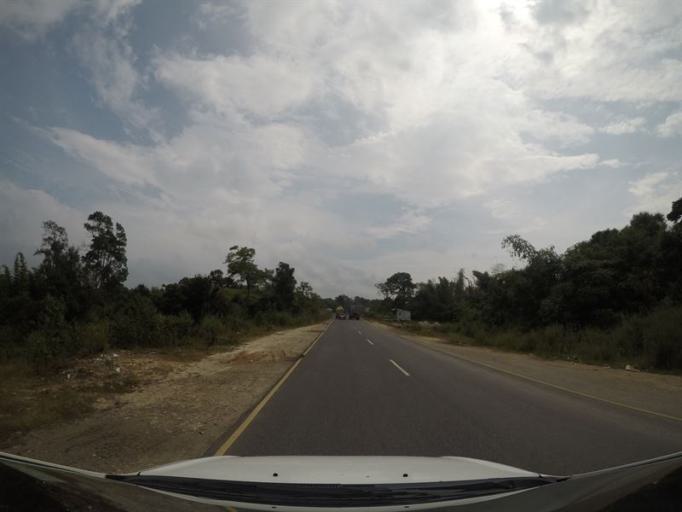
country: IN
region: Meghalaya
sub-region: East Khasi Hills
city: Shillong
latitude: 25.4870
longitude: 92.1917
